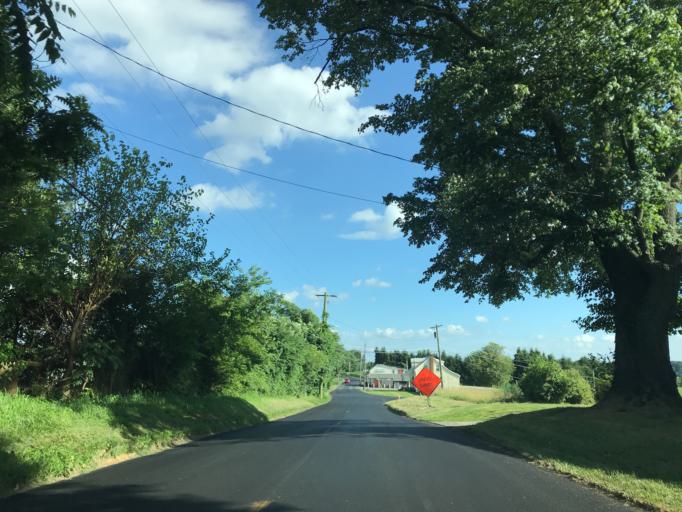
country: US
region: Maryland
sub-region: Carroll County
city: Hampstead
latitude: 39.6417
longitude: -76.8093
